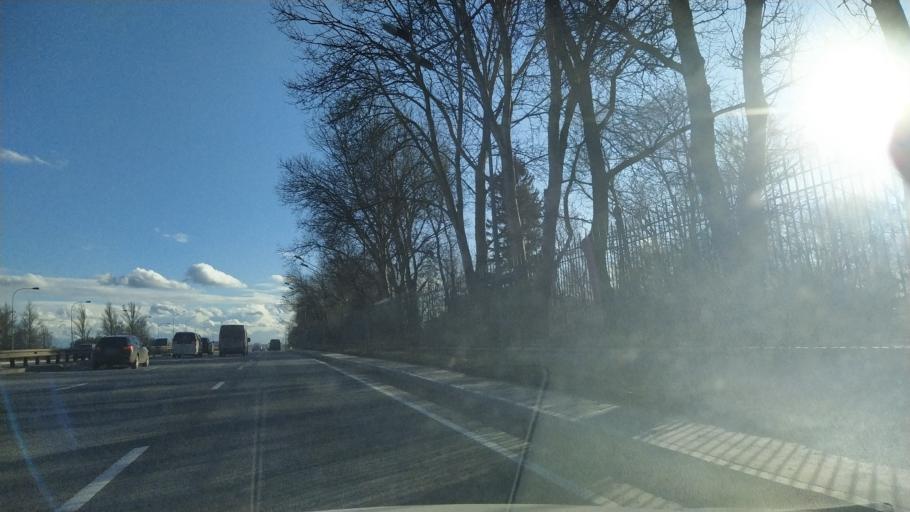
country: RU
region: St.-Petersburg
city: Aleksandrovskaya
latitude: 59.7689
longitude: 30.3318
